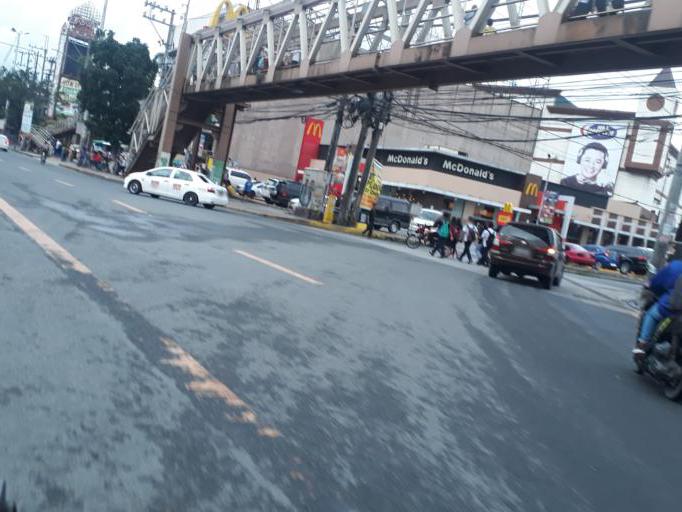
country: PH
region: Metro Manila
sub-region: Quezon City
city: Quezon City
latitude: 14.6774
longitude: 121.0833
